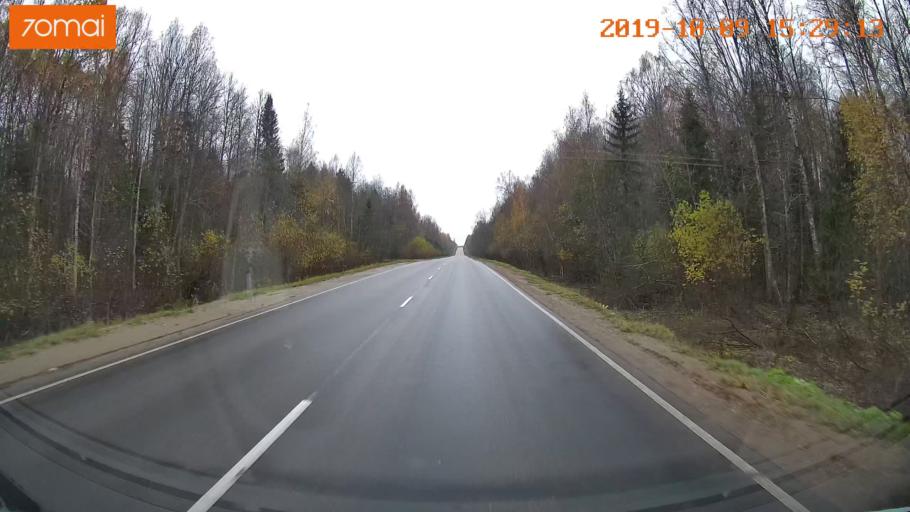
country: RU
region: Kostroma
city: Susanino
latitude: 57.9939
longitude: 41.3465
